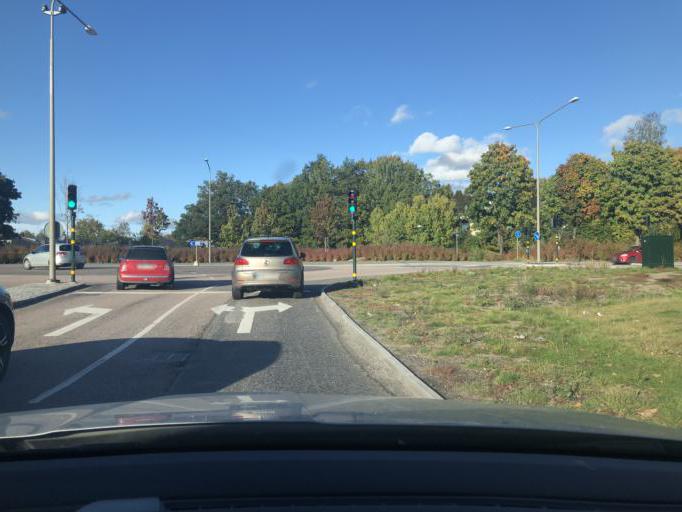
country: SE
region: Stockholm
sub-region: Huddinge Kommun
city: Segeltorp
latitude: 59.2681
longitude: 17.9021
